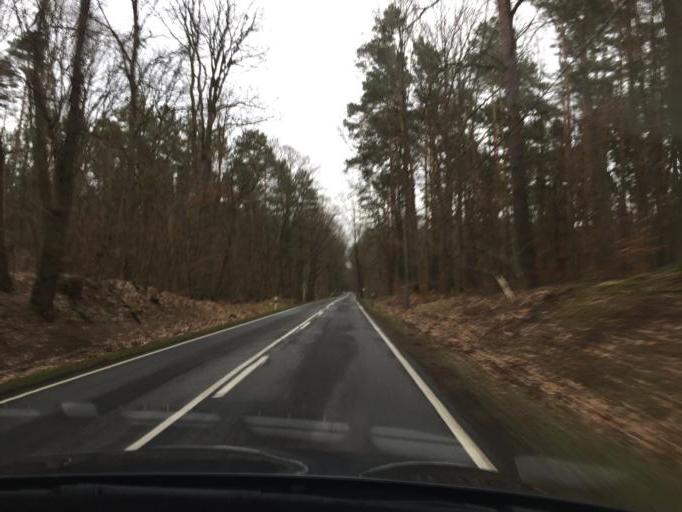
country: DE
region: Brandenburg
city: Jamlitz
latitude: 52.0753
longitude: 14.4560
